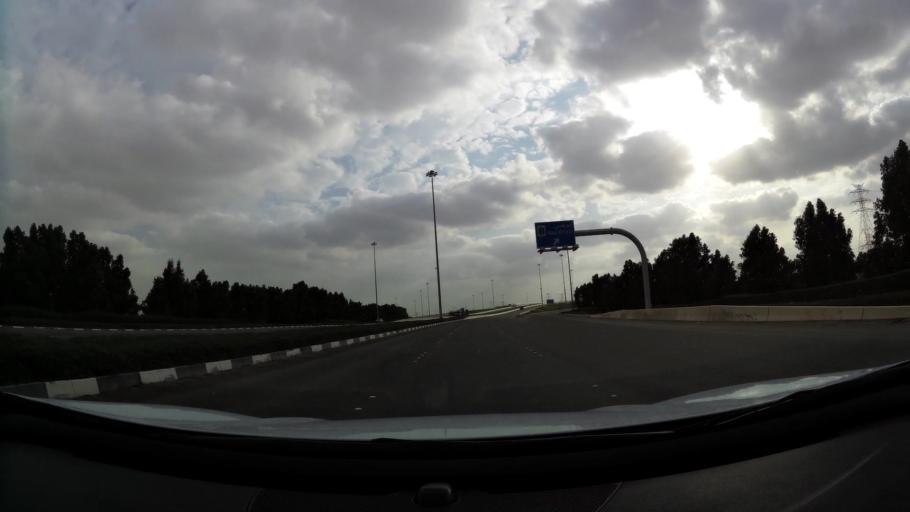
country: AE
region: Abu Dhabi
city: Abu Dhabi
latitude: 24.3317
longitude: 54.5891
